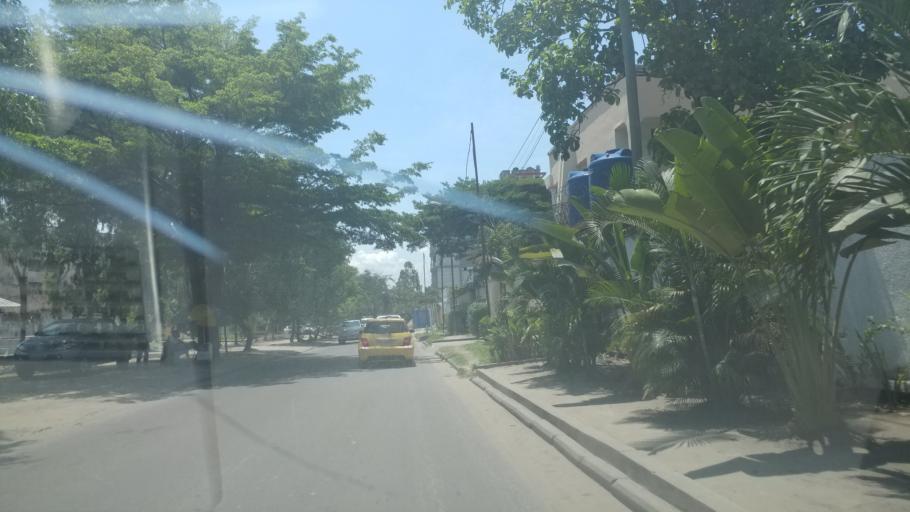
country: CD
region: Kinshasa
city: Kinshasa
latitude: -4.3188
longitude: 15.2823
